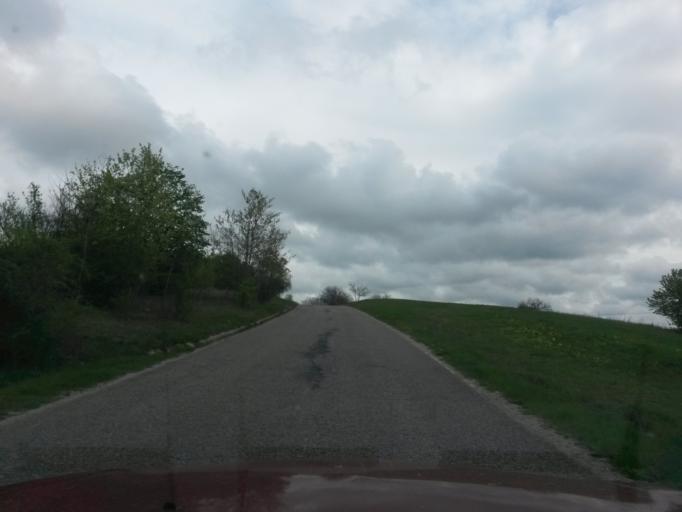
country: SK
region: Kosicky
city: Roznava
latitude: 48.5585
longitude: 20.5005
